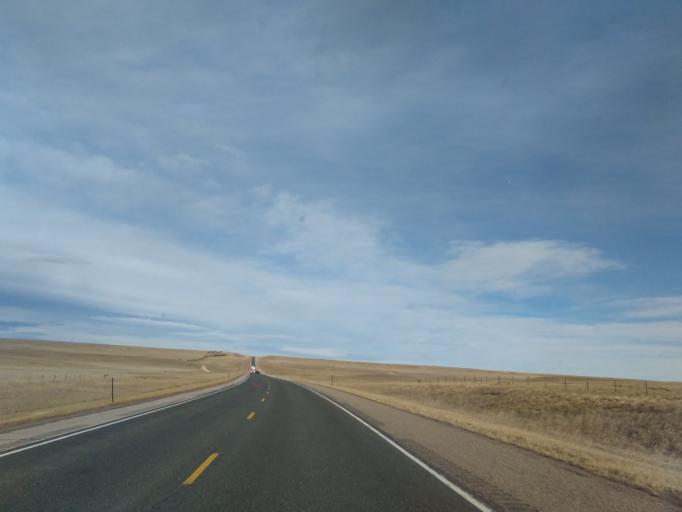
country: US
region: Wyoming
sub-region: Laramie County
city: Pine Bluffs
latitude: 41.5775
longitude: -104.2730
